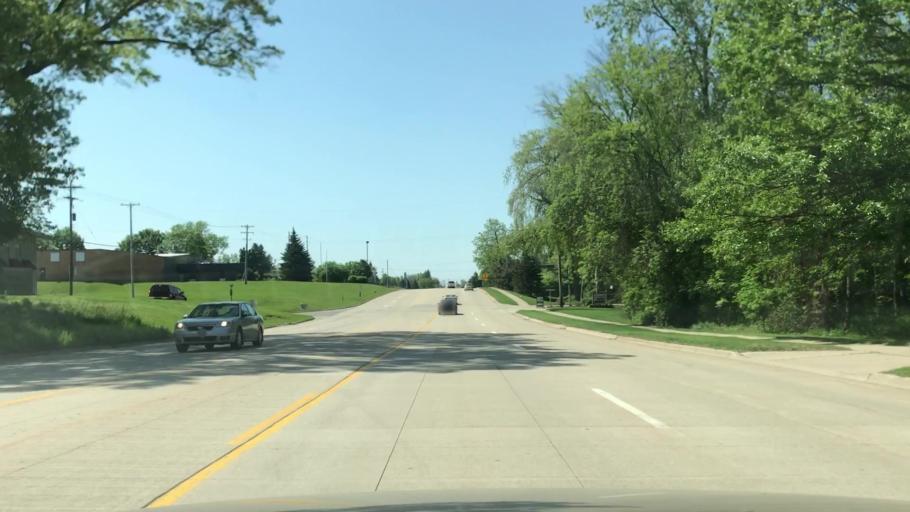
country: US
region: Michigan
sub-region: Kent County
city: East Grand Rapids
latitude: 42.9164
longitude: -85.5493
